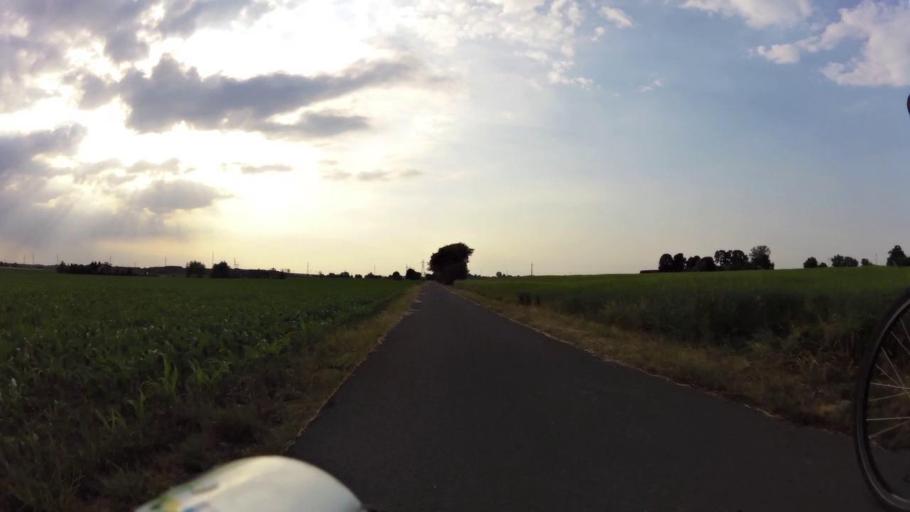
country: PL
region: Kujawsko-Pomorskie
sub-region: Powiat chelminski
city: Unislaw
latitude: 53.1771
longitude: 18.4121
